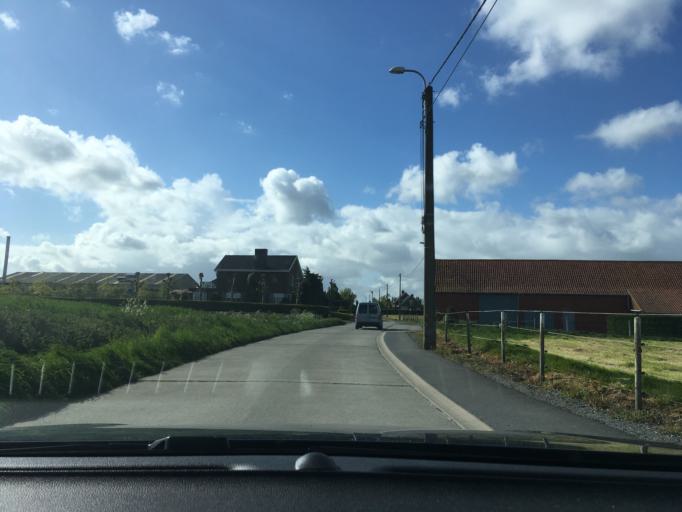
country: BE
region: Flanders
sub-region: Provincie West-Vlaanderen
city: Hooglede
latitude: 50.9997
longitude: 3.0770
